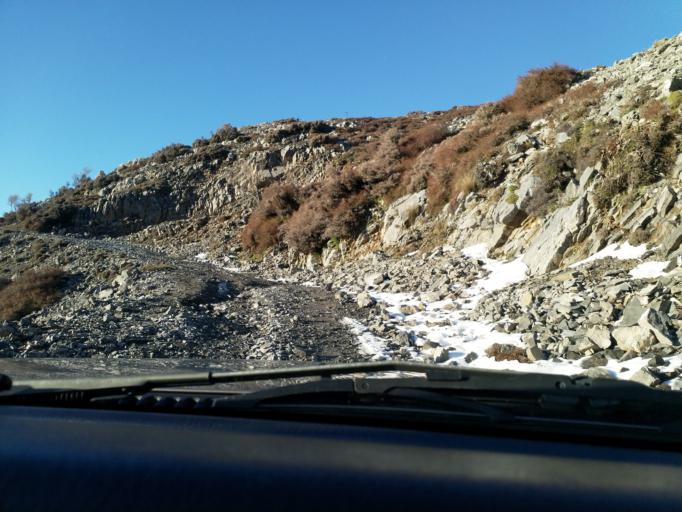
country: GR
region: Crete
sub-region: Nomos Chanias
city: Perivolia
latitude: 35.3215
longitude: 23.9290
